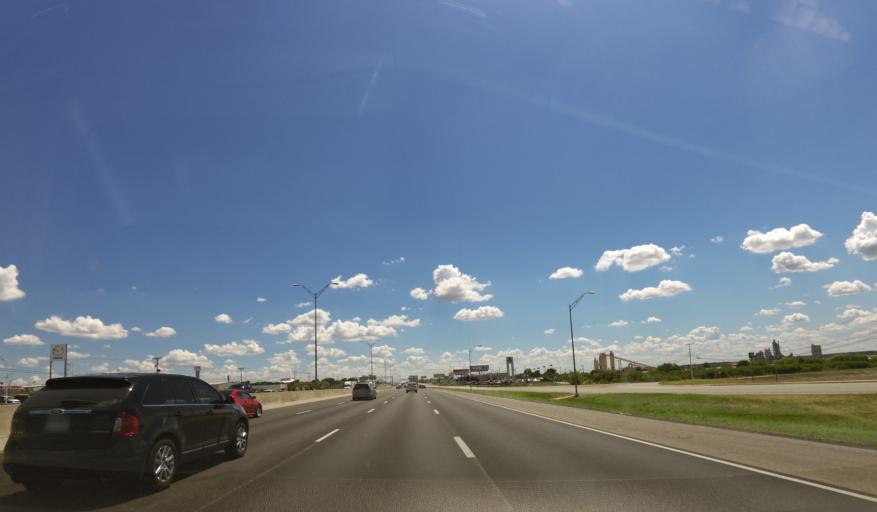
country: US
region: Texas
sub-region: Comal County
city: New Braunfels
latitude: 29.6731
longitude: -98.1566
